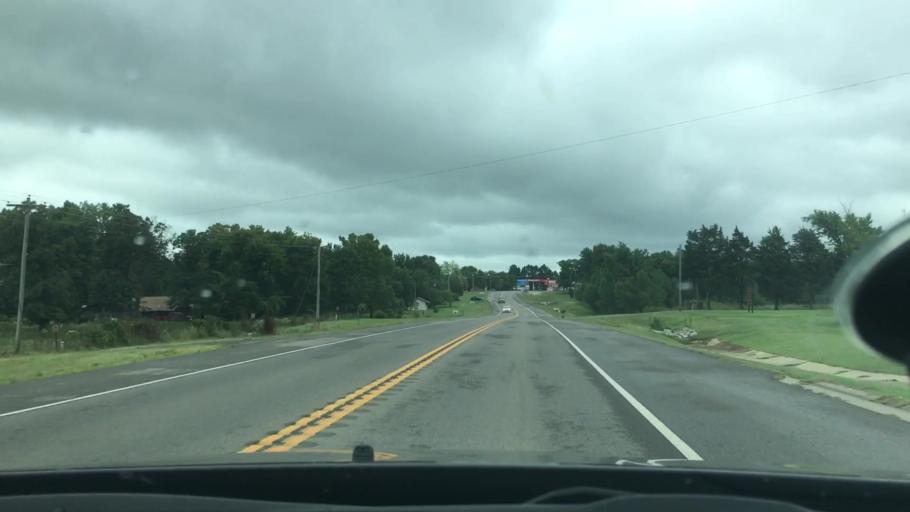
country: US
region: Oklahoma
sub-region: Sequoyah County
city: Vian
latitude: 35.6048
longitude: -94.9762
